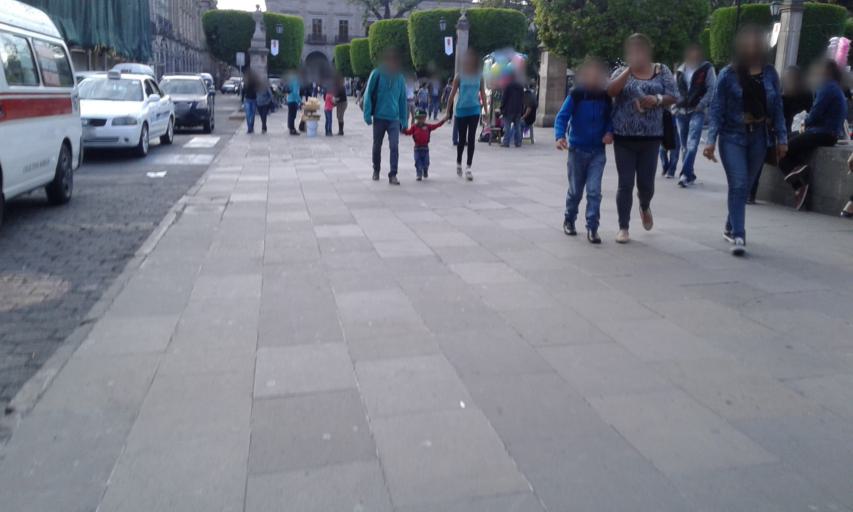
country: MX
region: Michoacan
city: Morelia
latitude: 19.7019
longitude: -101.1930
